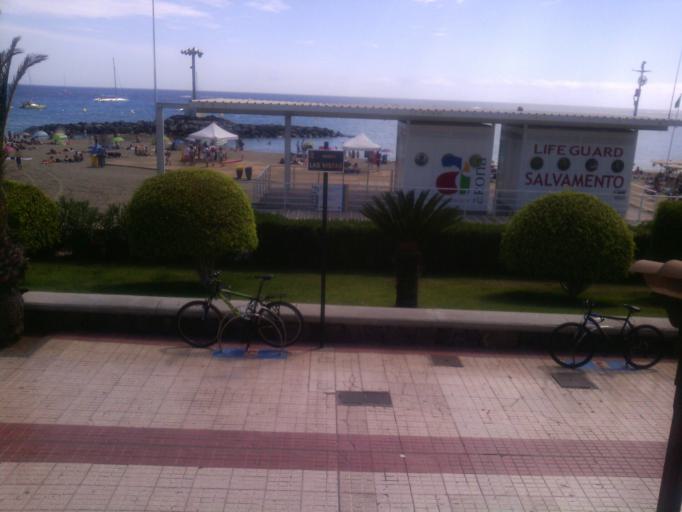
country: ES
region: Canary Islands
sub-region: Provincia de Santa Cruz de Tenerife
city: Playa de las Americas
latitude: 28.0523
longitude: -16.7230
